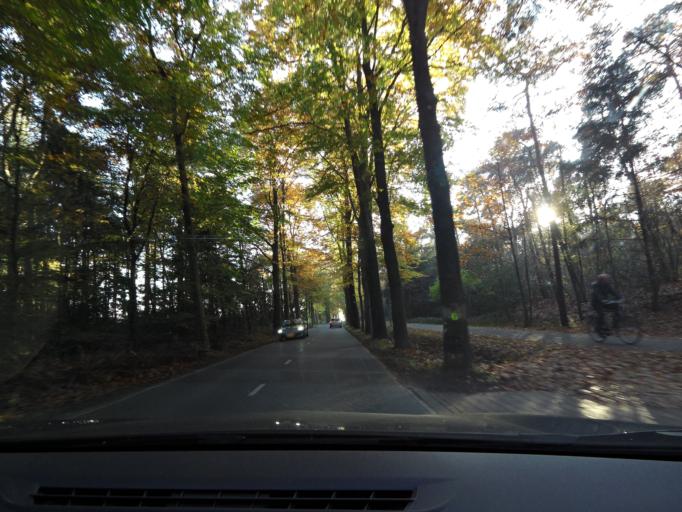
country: NL
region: North Brabant
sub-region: Gemeente Breda
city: Breda
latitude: 51.5336
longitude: 4.7725
